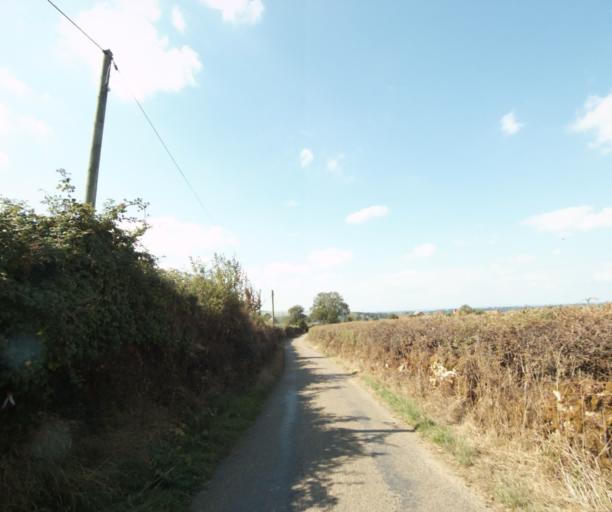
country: FR
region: Bourgogne
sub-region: Departement de Saone-et-Loire
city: Charolles
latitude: 46.3818
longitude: 4.2305
